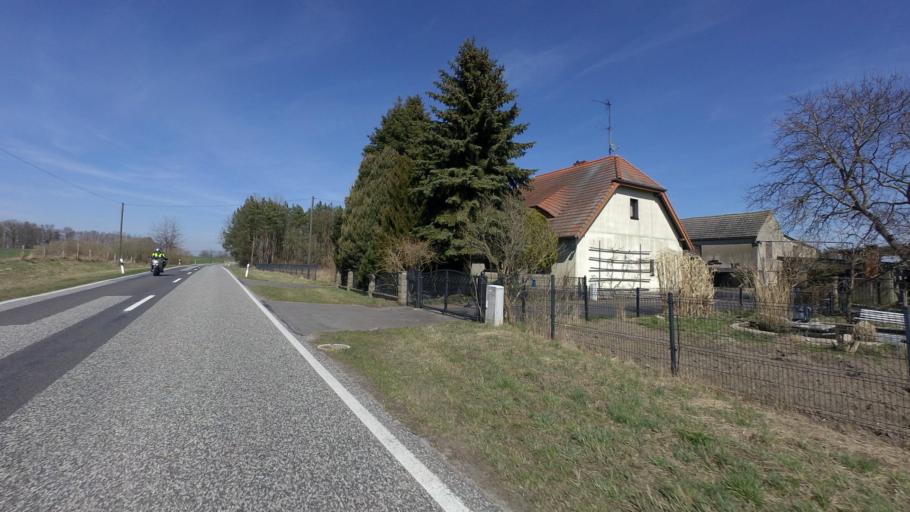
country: DE
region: Brandenburg
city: Furstenwalde
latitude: 52.4149
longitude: 14.0461
